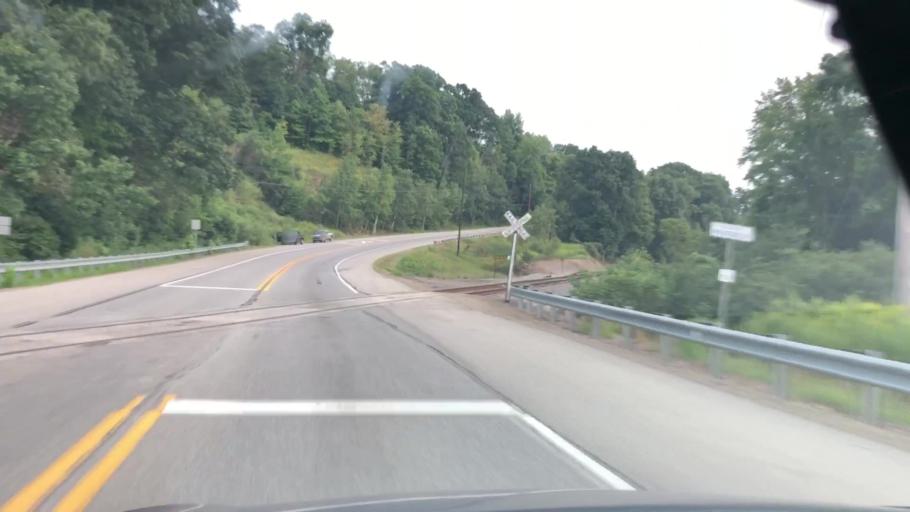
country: US
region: Pennsylvania
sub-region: Venango County
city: Hasson Heights
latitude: 41.4782
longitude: -79.6923
